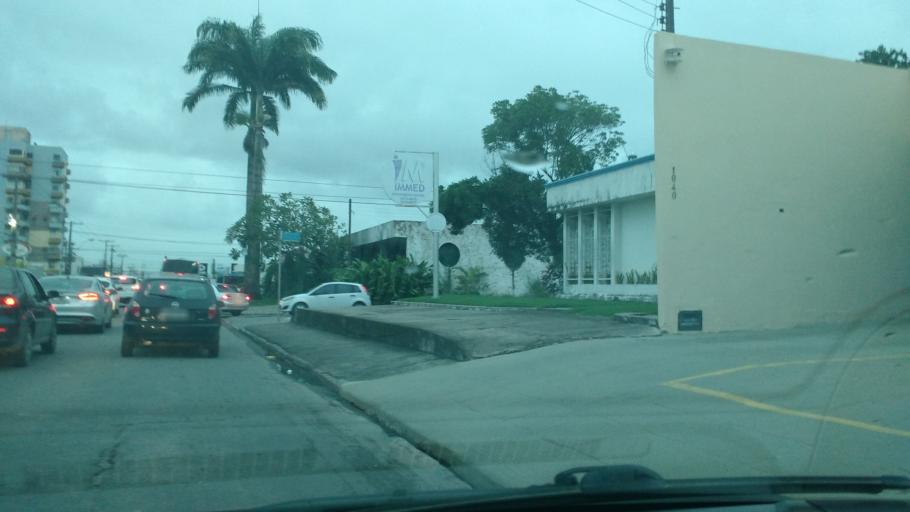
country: BR
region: Alagoas
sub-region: Maceio
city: Maceio
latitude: -9.6274
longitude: -35.7354
